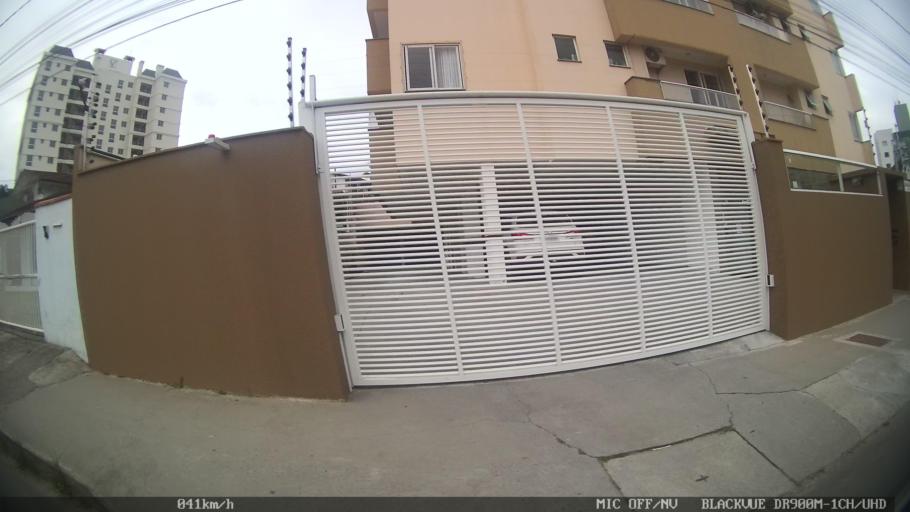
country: BR
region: Santa Catarina
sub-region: Joinville
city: Joinville
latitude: -26.2762
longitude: -48.8652
